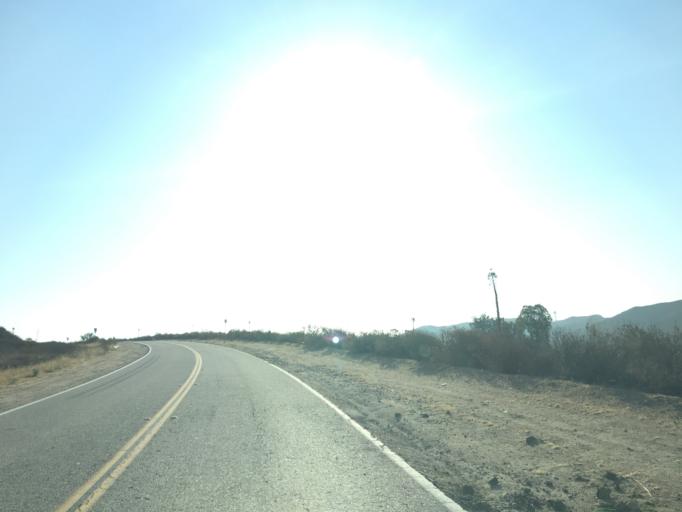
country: US
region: California
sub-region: Los Angeles County
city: Valencia
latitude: 34.4275
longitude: -118.6333
